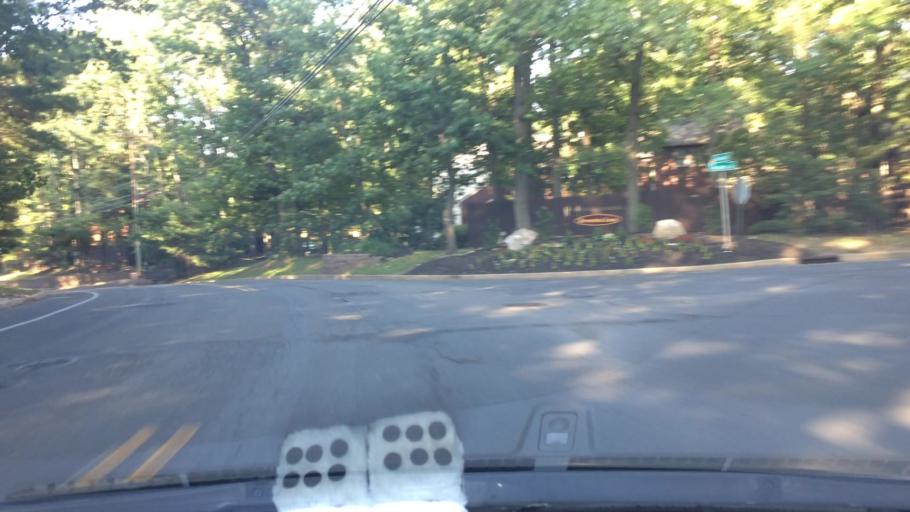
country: US
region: New Jersey
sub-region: Gloucester County
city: Turnersville
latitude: 39.7621
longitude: -75.0347
